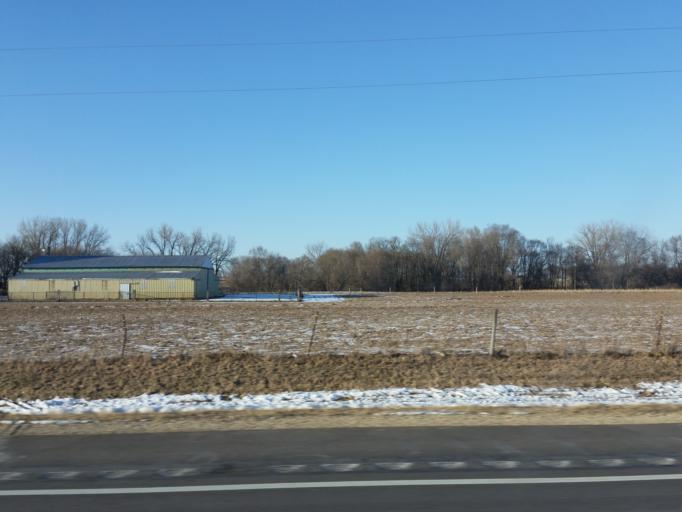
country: US
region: Minnesota
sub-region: Dakota County
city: Farmington
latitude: 44.6593
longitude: -93.0388
